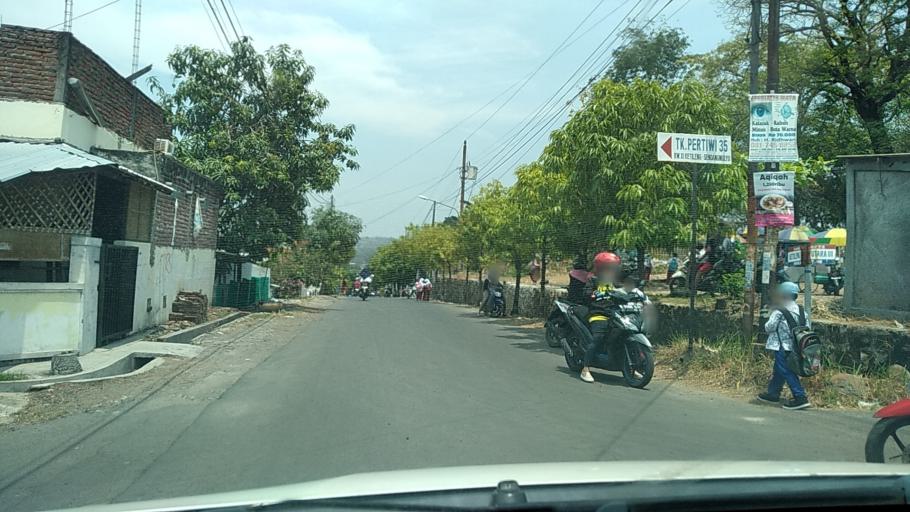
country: ID
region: Central Java
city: Mranggen
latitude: -7.0286
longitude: 110.4701
